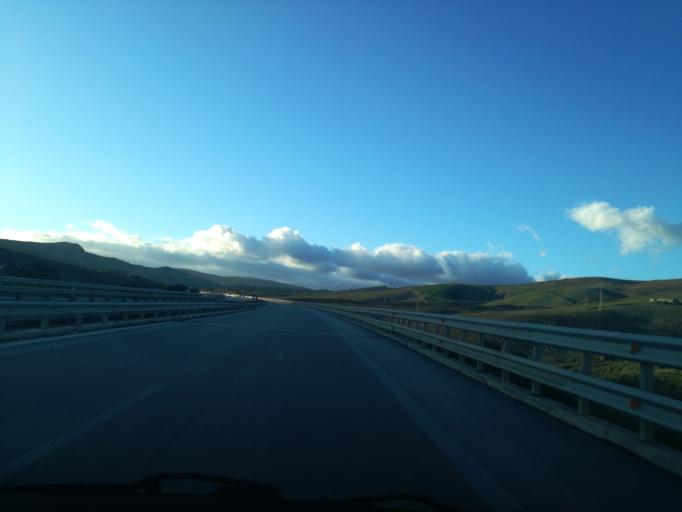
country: IT
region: Sicily
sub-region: Palermo
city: Castellana Sicula
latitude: 37.7428
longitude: 13.9937
